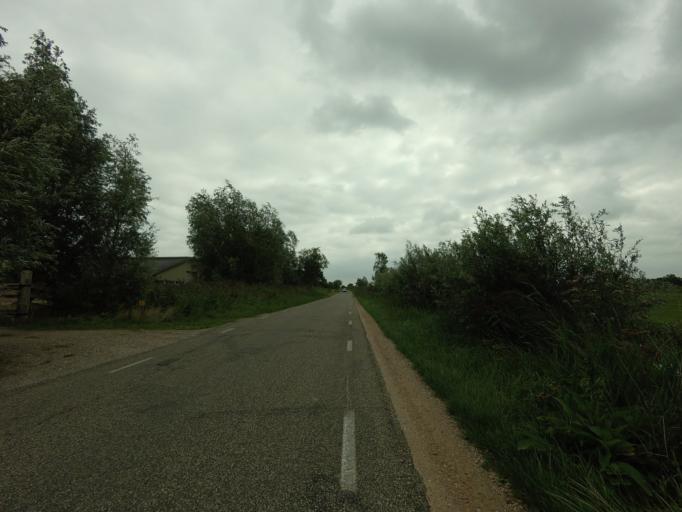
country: NL
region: Utrecht
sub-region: Stichtse Vecht
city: Breukelen
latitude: 52.2000
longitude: 4.9351
